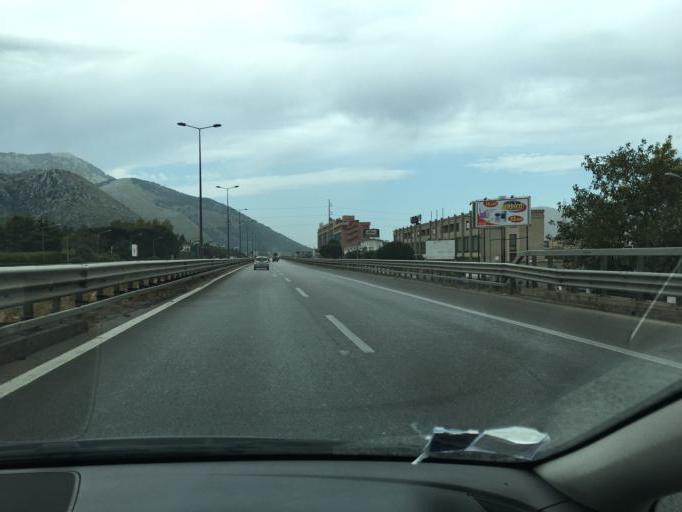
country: IT
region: Sicily
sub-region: Palermo
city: Palermo
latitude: 38.1599
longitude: 13.3126
